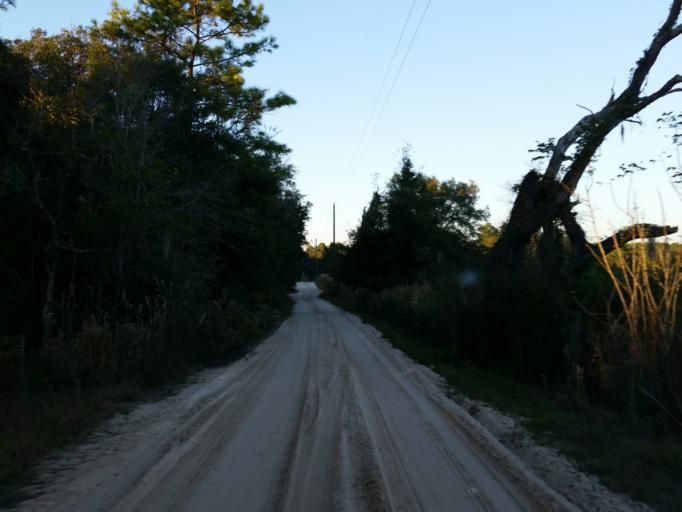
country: US
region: Florida
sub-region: Hernando County
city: Hill 'n Dale
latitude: 28.5284
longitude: -82.2508
